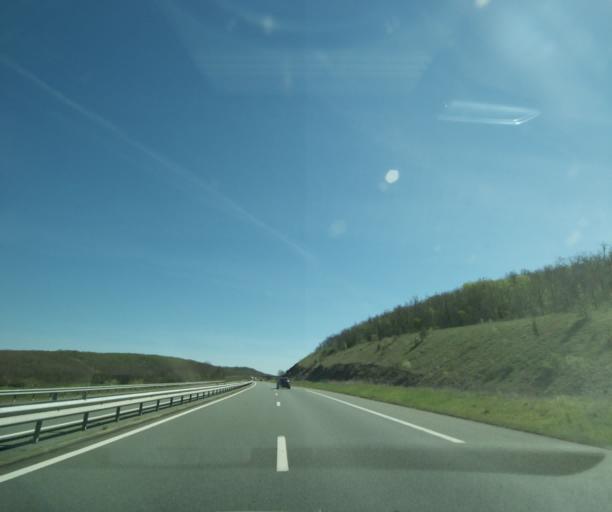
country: FR
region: Midi-Pyrenees
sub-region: Departement du Lot
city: Le Vigan
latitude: 44.7796
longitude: 1.5325
